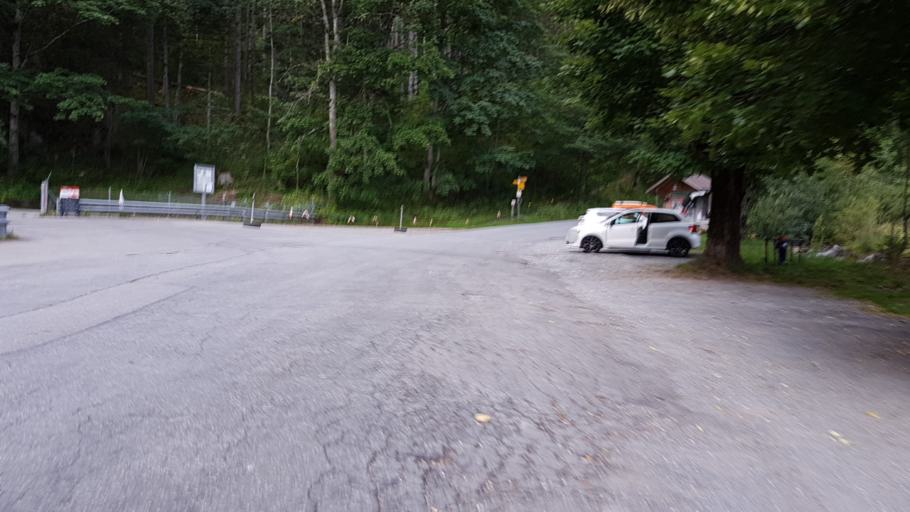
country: CH
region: Bern
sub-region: Frutigen-Niedersimmental District
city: Kandersteg
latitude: 46.4748
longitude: 7.6605
